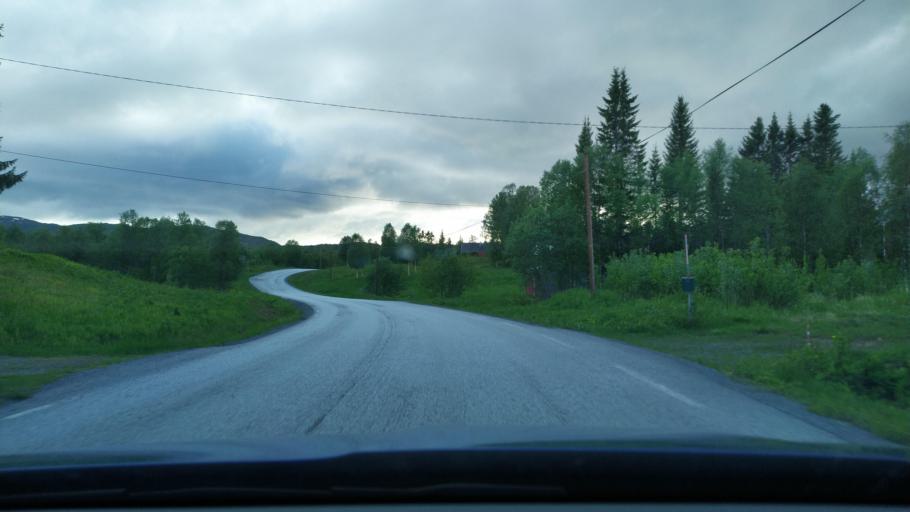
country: NO
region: Troms
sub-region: Dyroy
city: Brostadbotn
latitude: 69.0551
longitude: 17.7974
